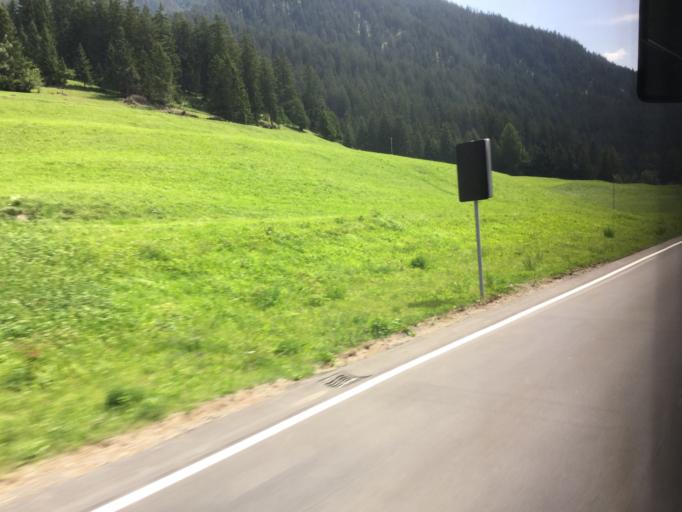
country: CH
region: Grisons
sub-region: Albula District
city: Tiefencastel
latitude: 46.6275
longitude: 9.5846
